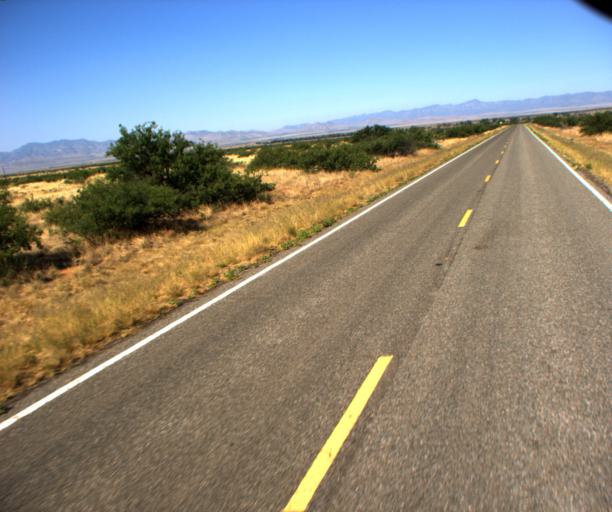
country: US
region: Arizona
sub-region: Graham County
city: Swift Trail Junction
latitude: 32.5832
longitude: -109.9433
